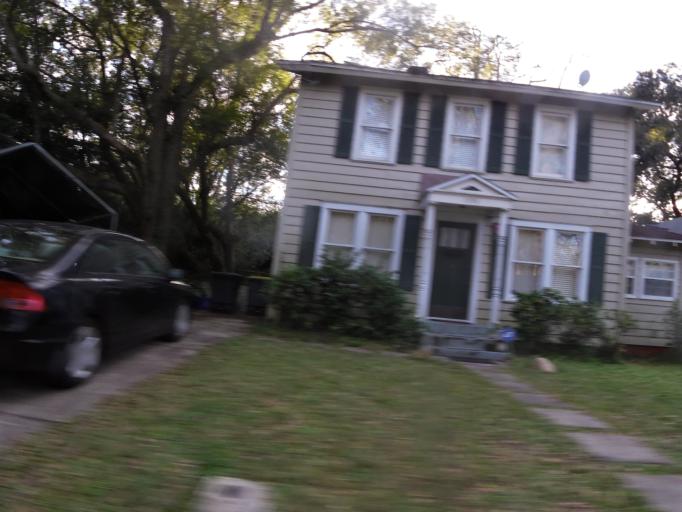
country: US
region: Florida
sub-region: Duval County
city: Jacksonville
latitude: 30.3007
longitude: -81.7129
